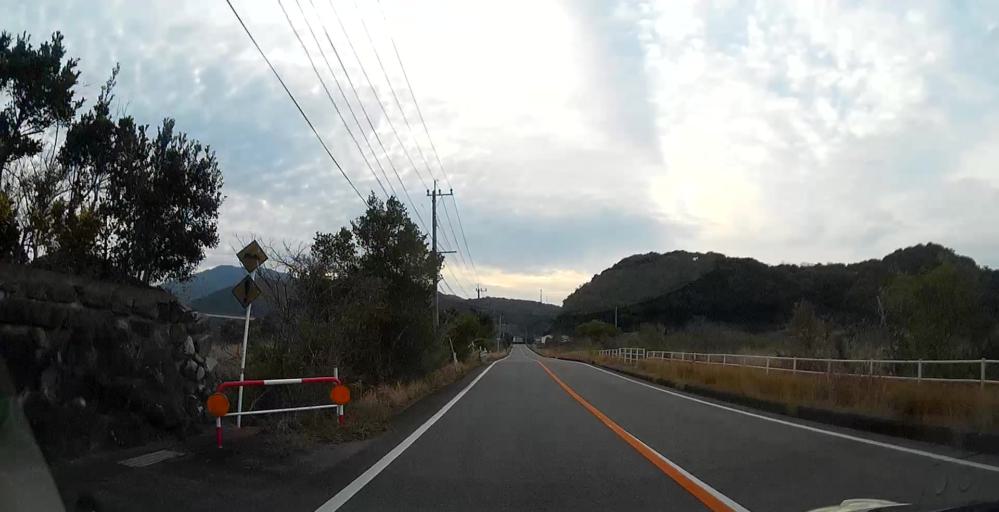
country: JP
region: Kumamoto
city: Hondo
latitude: 32.5092
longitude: 130.3800
